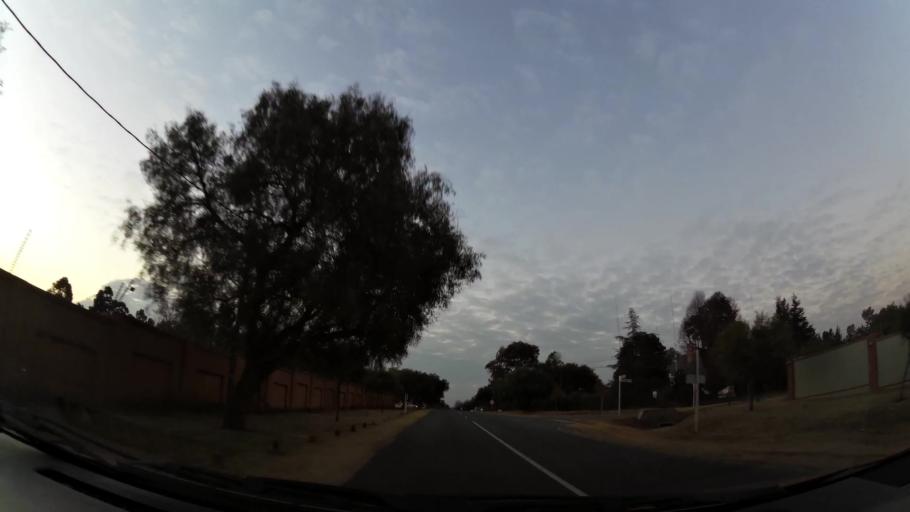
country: ZA
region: Gauteng
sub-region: City of Johannesburg Metropolitan Municipality
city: Diepsloot
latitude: -25.9684
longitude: 28.0652
